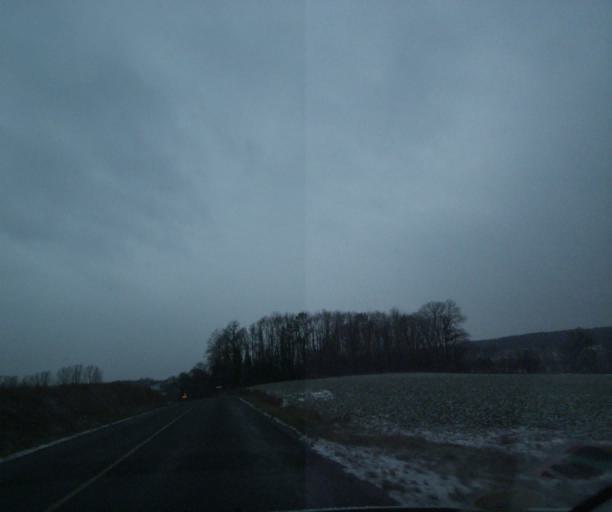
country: FR
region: Champagne-Ardenne
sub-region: Departement de la Haute-Marne
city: Wassy
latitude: 48.4186
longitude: 4.9464
